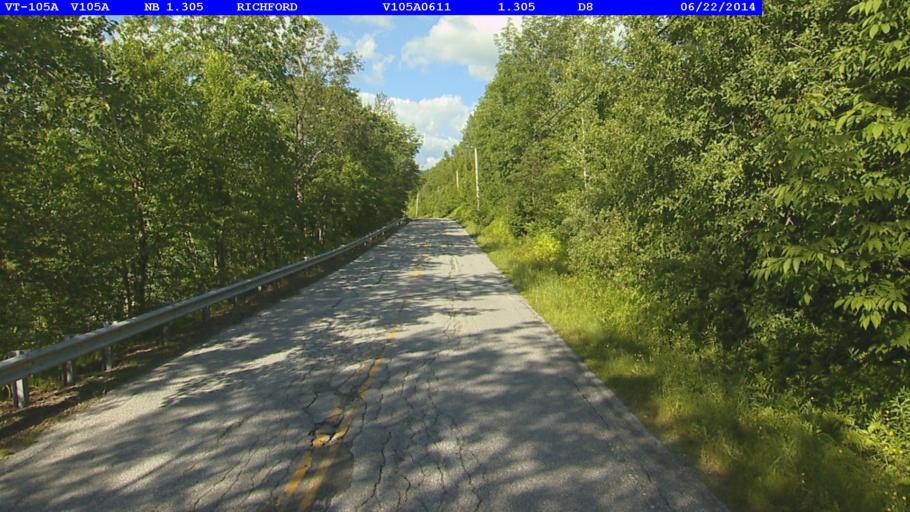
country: US
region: Vermont
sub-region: Franklin County
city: Richford
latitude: 45.0065
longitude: -72.5923
